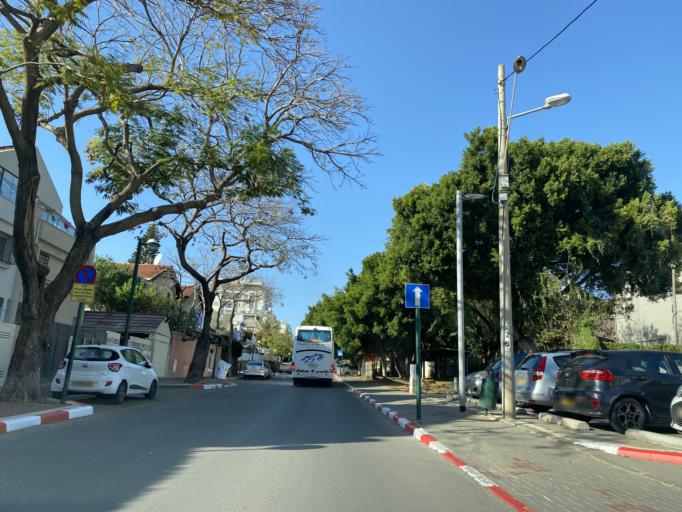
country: IL
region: Central District
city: Kfar Saba
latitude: 32.1785
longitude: 34.9154
